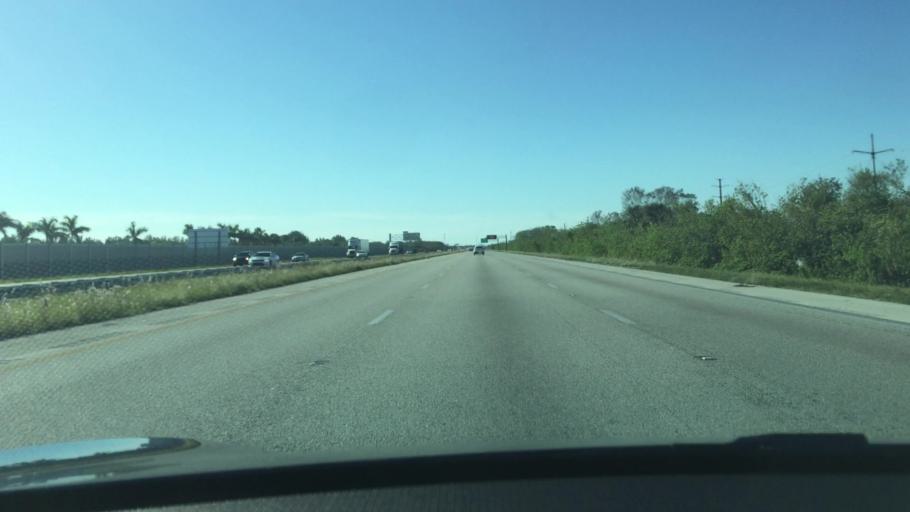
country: US
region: Florida
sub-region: Brevard County
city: June Park
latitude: 28.1063
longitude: -80.7061
